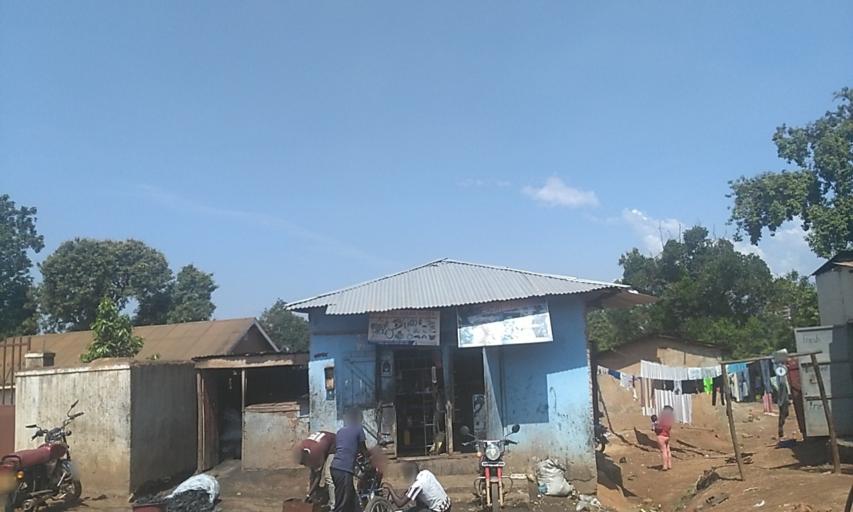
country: UG
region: Central Region
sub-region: Wakiso District
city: Kireka
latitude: 0.3628
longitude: 32.6069
